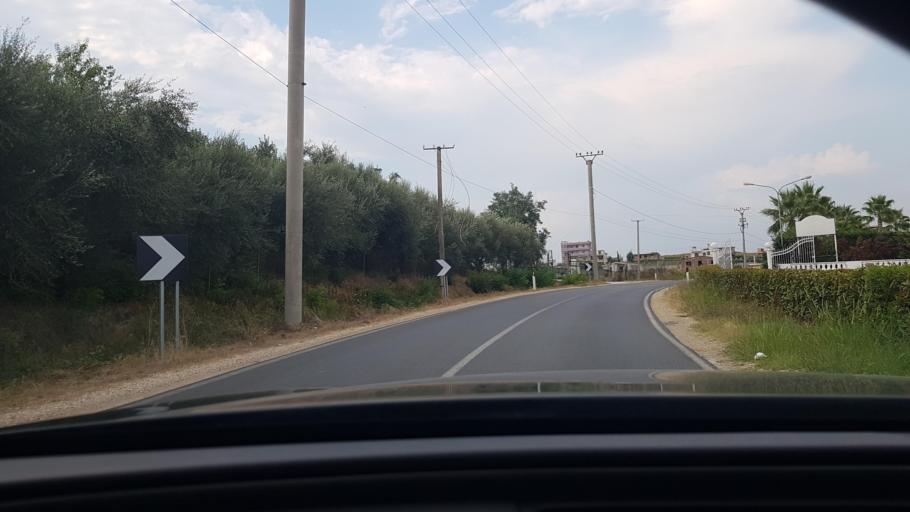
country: AL
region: Durres
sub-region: Rrethi i Durresit
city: Katundi i Ri
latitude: 41.4145
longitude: 19.5457
